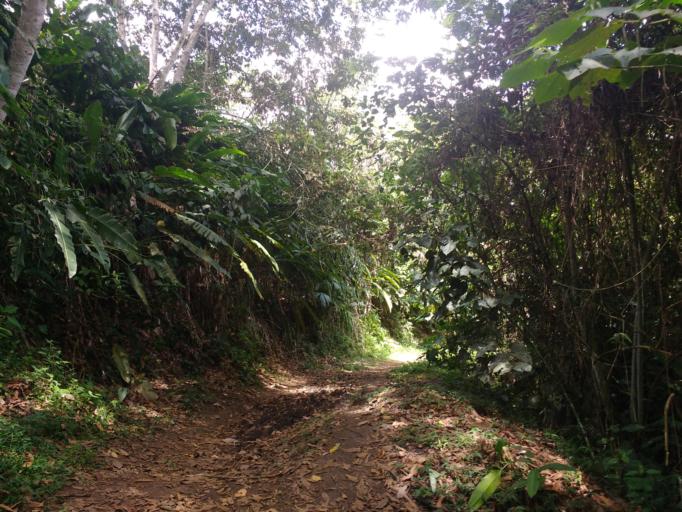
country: CO
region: Valle del Cauca
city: Alcala
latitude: 4.6749
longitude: -75.8138
